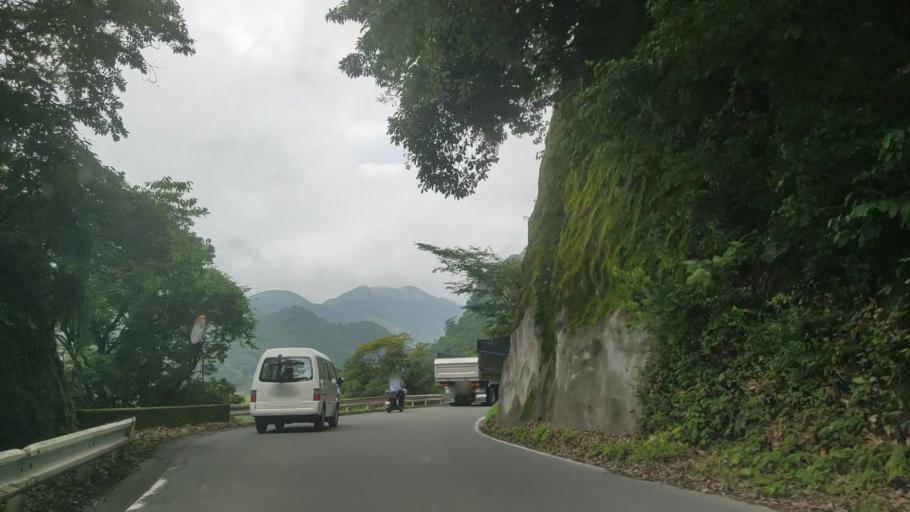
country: JP
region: Shizuoka
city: Fujinomiya
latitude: 35.2248
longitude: 138.5405
